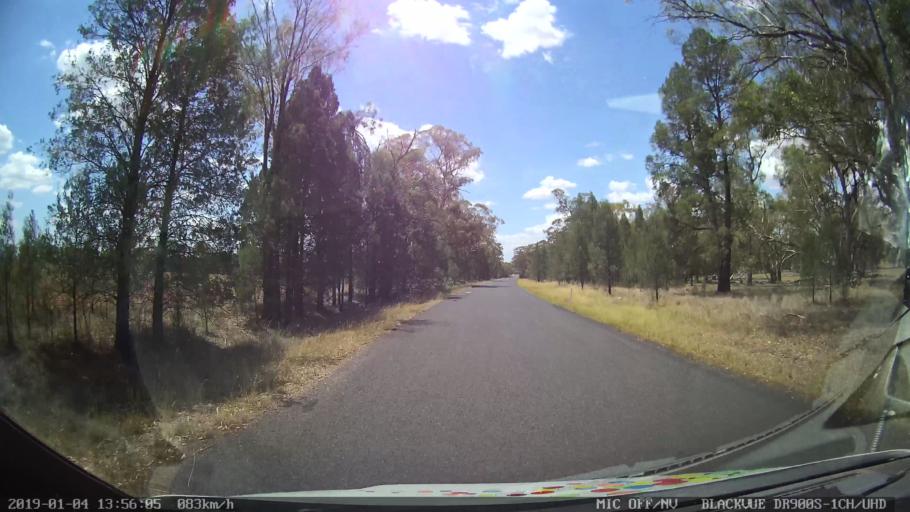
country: AU
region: New South Wales
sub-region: Dubbo Municipality
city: Dubbo
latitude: -32.3550
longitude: 148.5914
